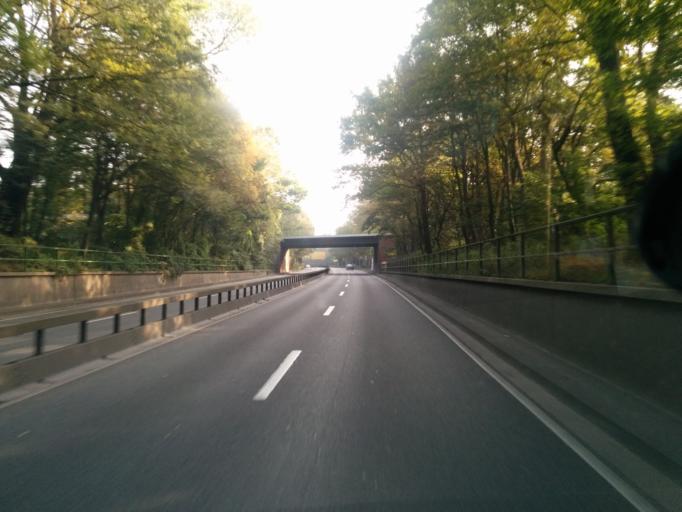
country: DE
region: Lower Saxony
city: Laatzen
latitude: 52.3442
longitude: 9.7794
